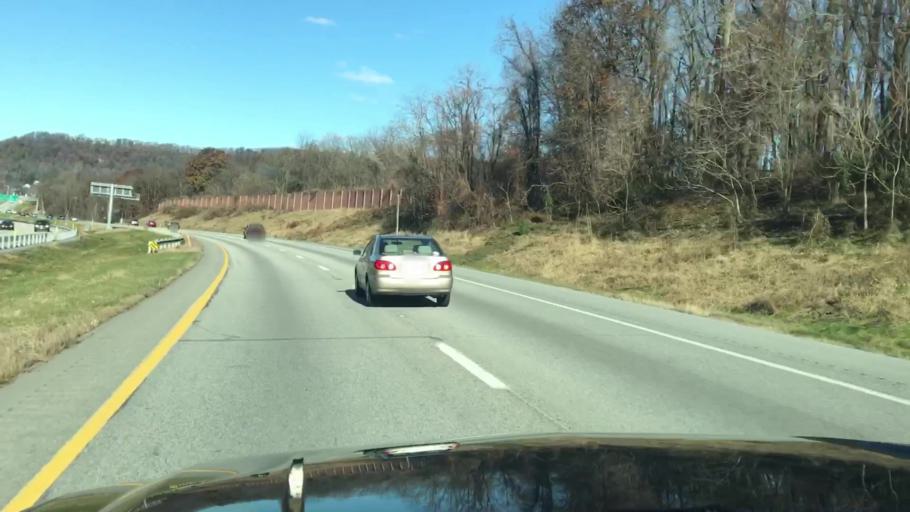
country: US
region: Pennsylvania
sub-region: Dauphin County
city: Harrisburg
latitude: 40.3200
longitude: -76.8834
